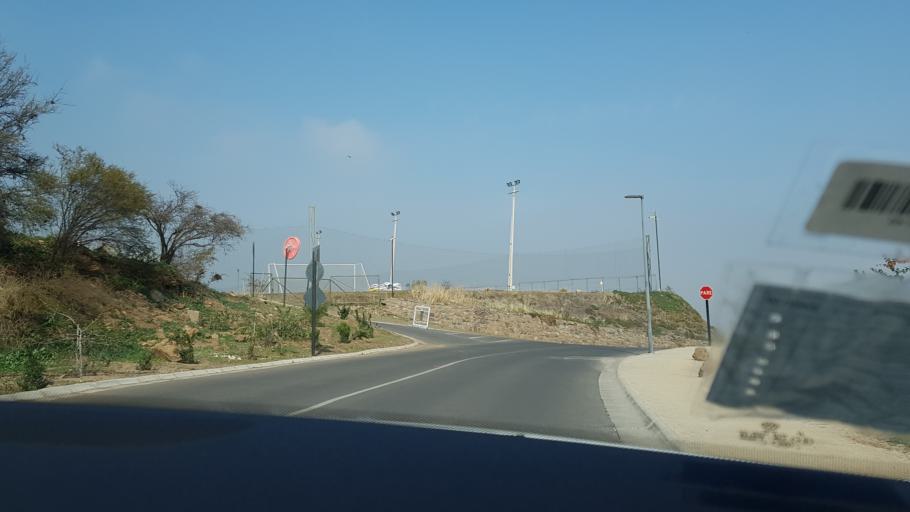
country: CL
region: Santiago Metropolitan
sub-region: Provincia de Santiago
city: Villa Presidente Frei, Nunoa, Santiago, Chile
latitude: -33.4771
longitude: -70.5162
